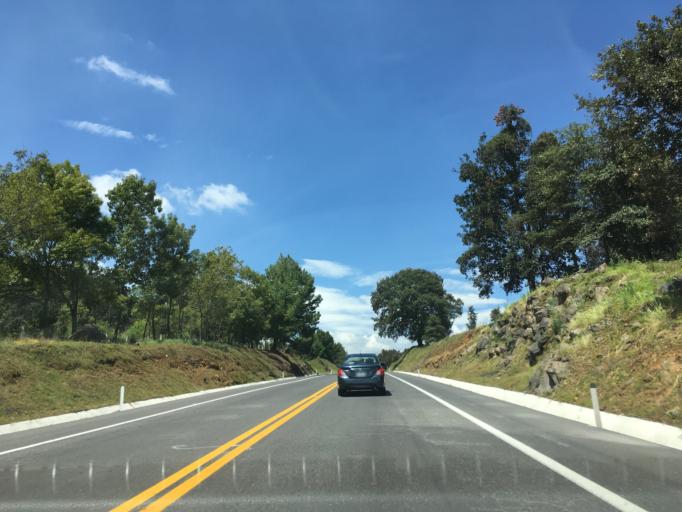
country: MX
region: Michoacan
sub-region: Patzcuaro
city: Santa Ana Chapitiro
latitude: 19.5020
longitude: -101.6414
